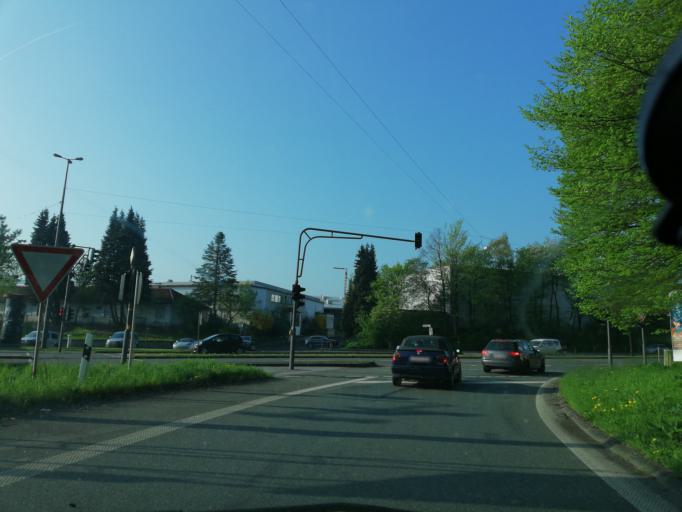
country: DE
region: North Rhine-Westphalia
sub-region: Regierungsbezirk Arnsberg
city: Schwelm
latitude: 51.2829
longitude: 7.2530
